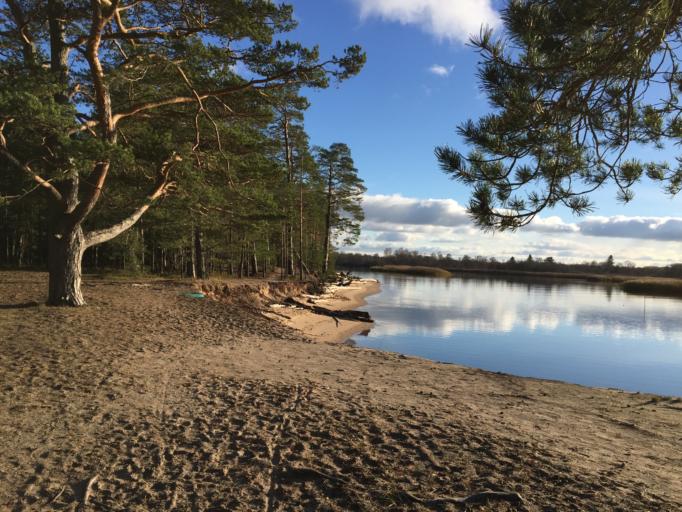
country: LV
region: Carnikava
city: Carnikava
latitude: 57.1574
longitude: 24.2726
